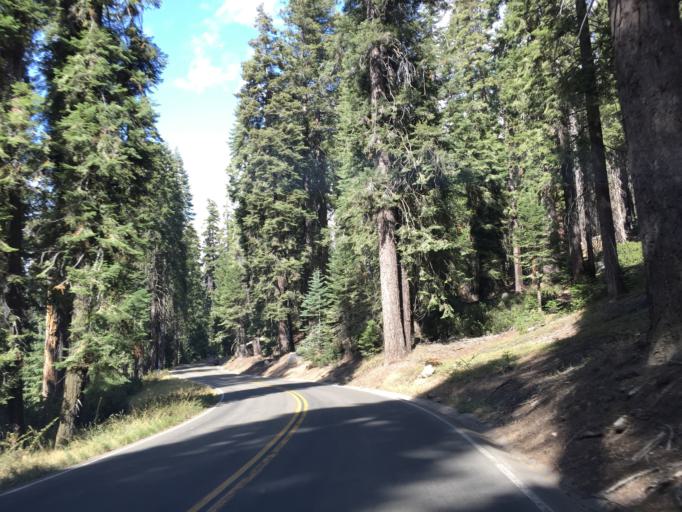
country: US
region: California
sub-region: Tulare County
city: Three Rivers
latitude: 36.5893
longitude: -118.7482
